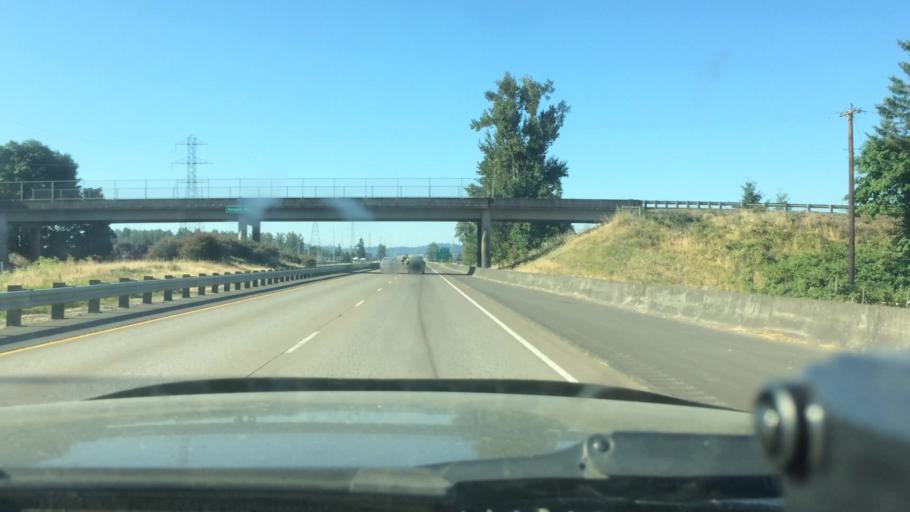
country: US
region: Oregon
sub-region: Lane County
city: Coburg
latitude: 44.1036
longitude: -123.0446
